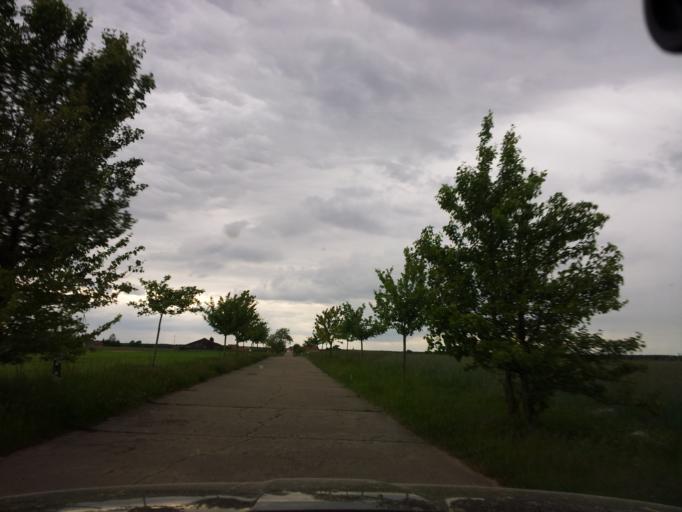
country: DE
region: Brandenburg
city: Niedergorsdorf
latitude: 52.0044
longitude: 12.9288
